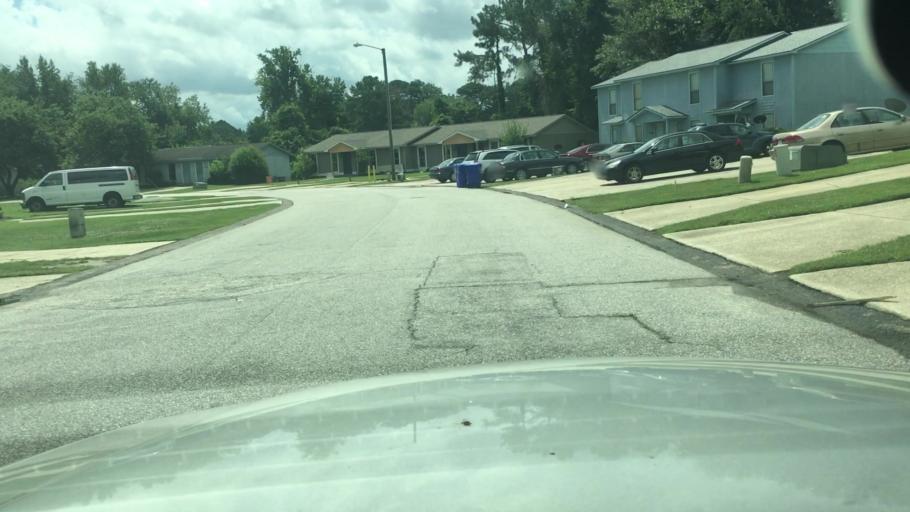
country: US
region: North Carolina
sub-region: Cumberland County
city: Hope Mills
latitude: 35.0343
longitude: -78.9765
